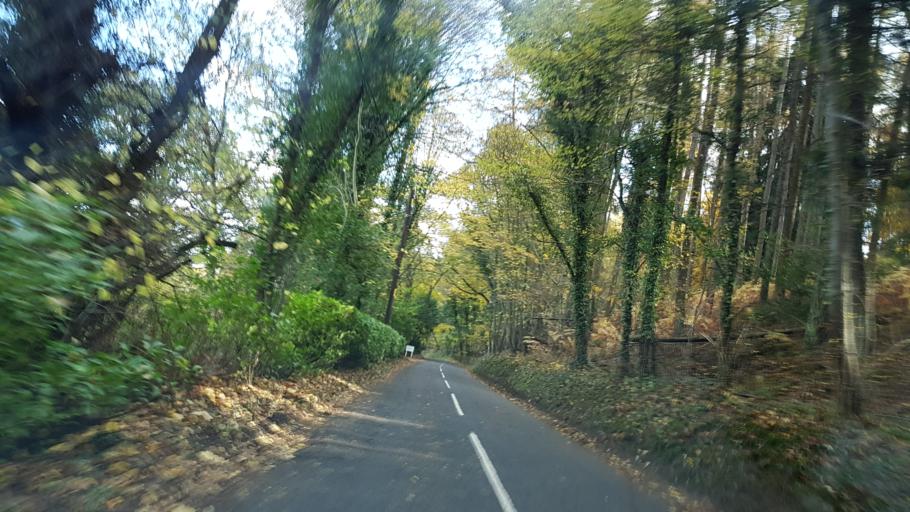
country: GB
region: England
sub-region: Surrey
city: Seale
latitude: 51.2225
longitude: -0.7123
